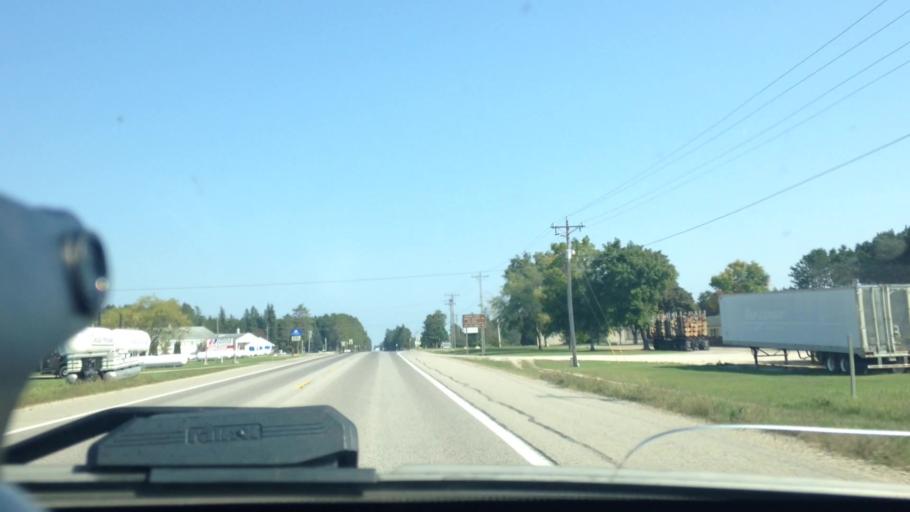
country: US
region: Michigan
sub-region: Luce County
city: Newberry
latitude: 46.3034
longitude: -85.4915
